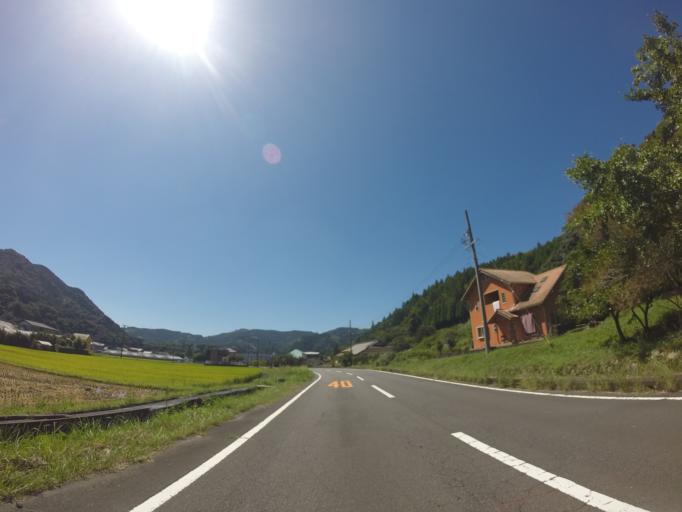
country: JP
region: Shizuoka
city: Fujieda
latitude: 34.9164
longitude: 138.2033
